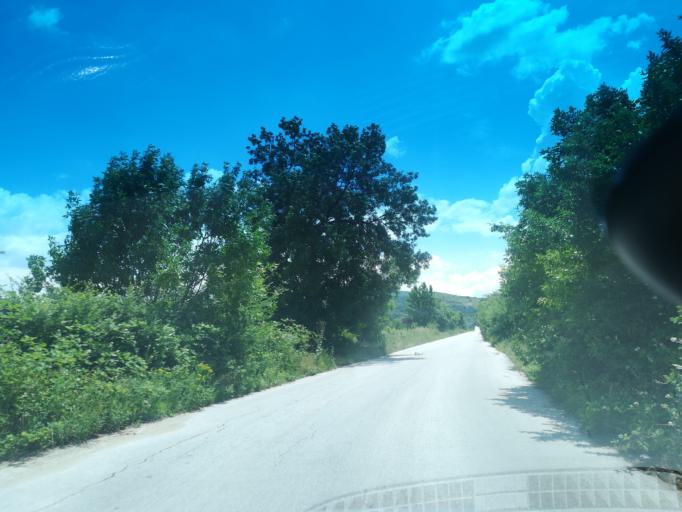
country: BG
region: Khaskovo
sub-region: Obshtina Mineralni Bani
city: Mineralni Bani
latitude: 41.9923
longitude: 25.2407
